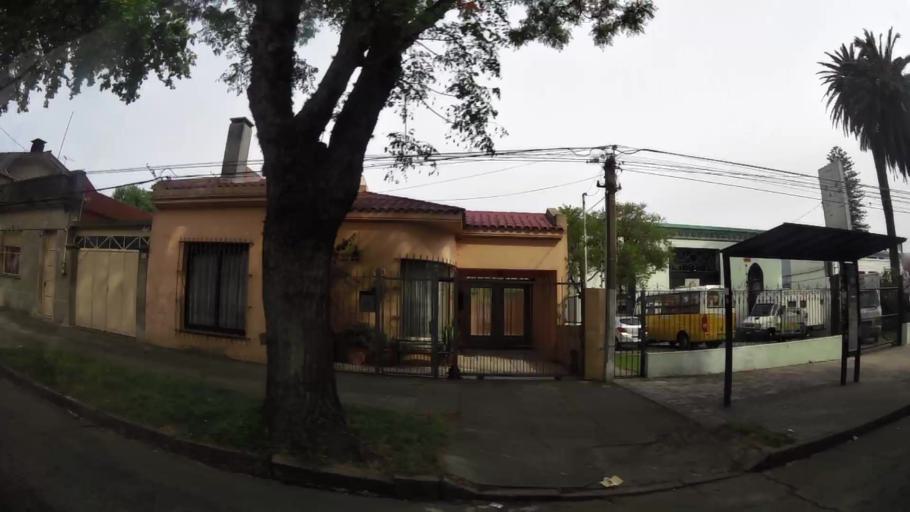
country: UY
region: Montevideo
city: Montevideo
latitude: -34.8688
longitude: -56.2076
